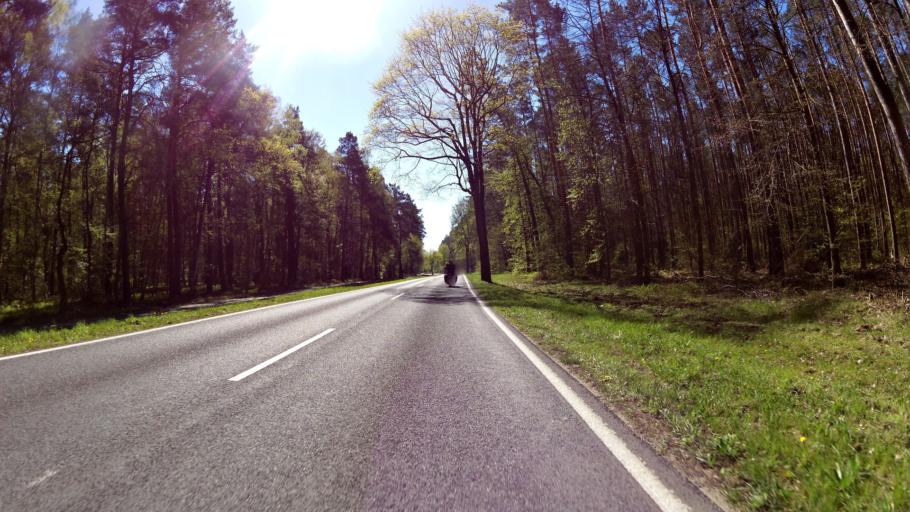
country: DE
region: Brandenburg
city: Bernau bei Berlin
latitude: 52.7104
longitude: 13.5348
